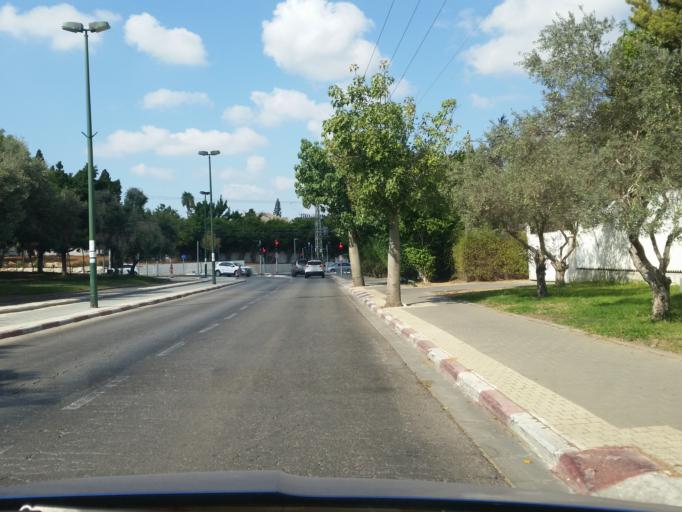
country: IL
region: Tel Aviv
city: Ramat HaSharon
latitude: 32.1181
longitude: 34.8343
